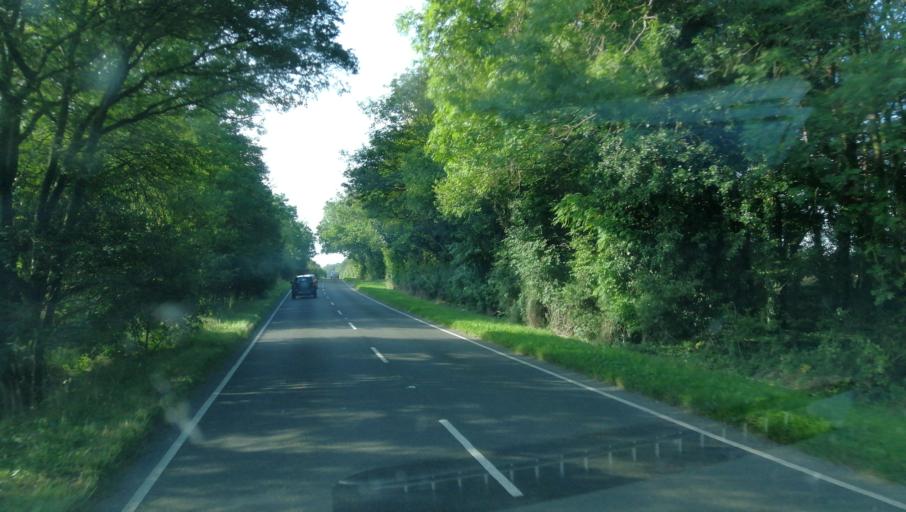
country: GB
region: England
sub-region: Oxfordshire
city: Woodstock
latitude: 51.9057
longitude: -1.3288
